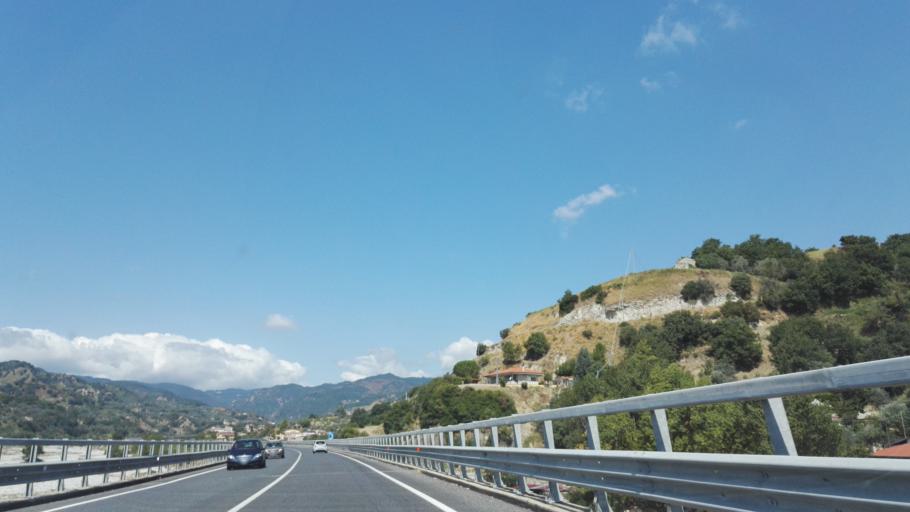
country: IT
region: Calabria
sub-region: Provincia di Reggio Calabria
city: Martone
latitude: 38.3416
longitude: 16.2742
